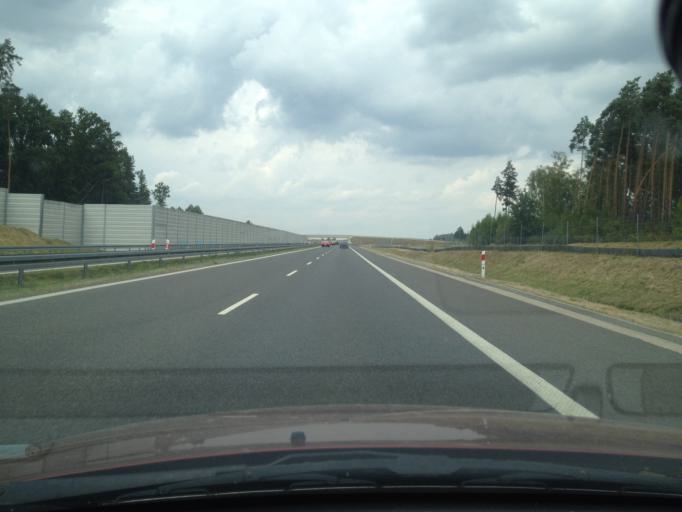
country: PL
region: West Pomeranian Voivodeship
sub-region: Powiat mysliborski
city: Mysliborz
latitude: 52.9714
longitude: 14.9106
